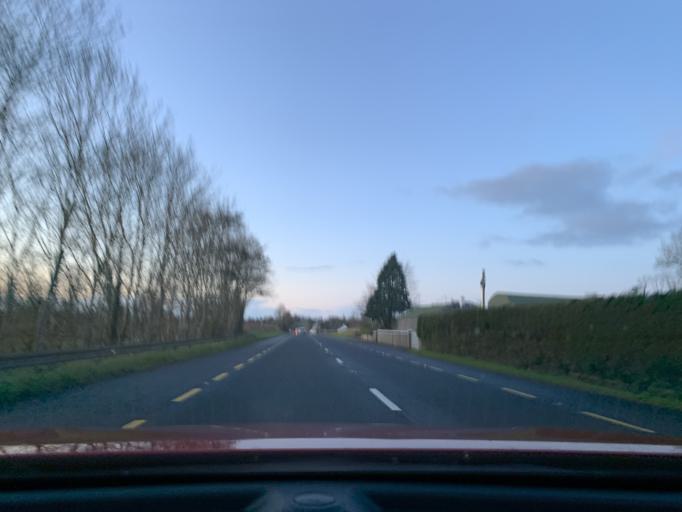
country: IE
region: Connaught
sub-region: County Leitrim
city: Carrick-on-Shannon
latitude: 53.9094
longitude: -7.9646
